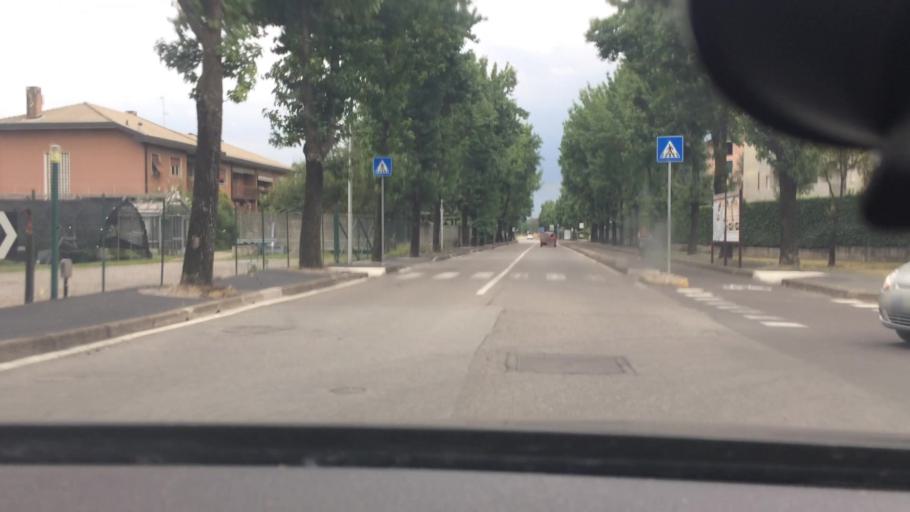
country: IT
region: Lombardy
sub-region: Citta metropolitana di Milano
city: Cerro Maggiore
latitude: 45.5917
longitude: 8.9601
